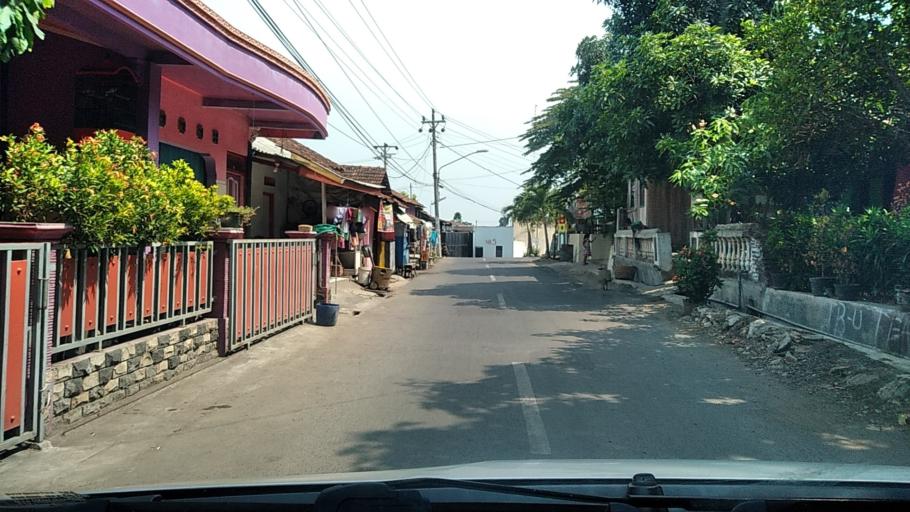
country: ID
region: Central Java
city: Semarang
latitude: -6.9800
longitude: 110.3437
